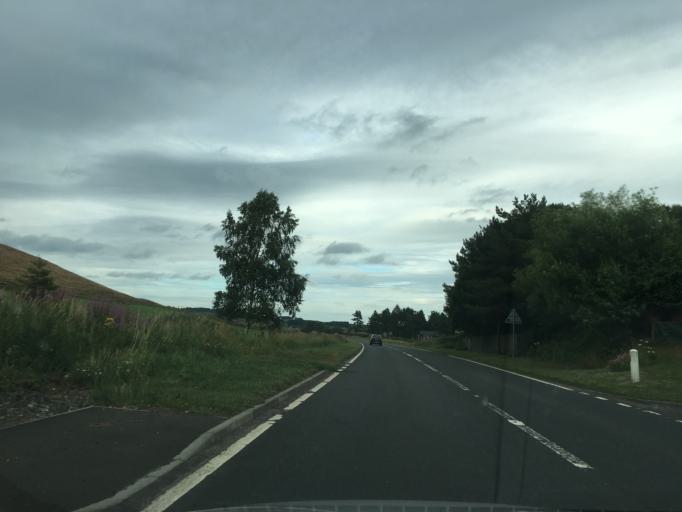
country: GB
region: Scotland
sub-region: The Scottish Borders
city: West Linton
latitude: 55.7162
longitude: -3.4135
